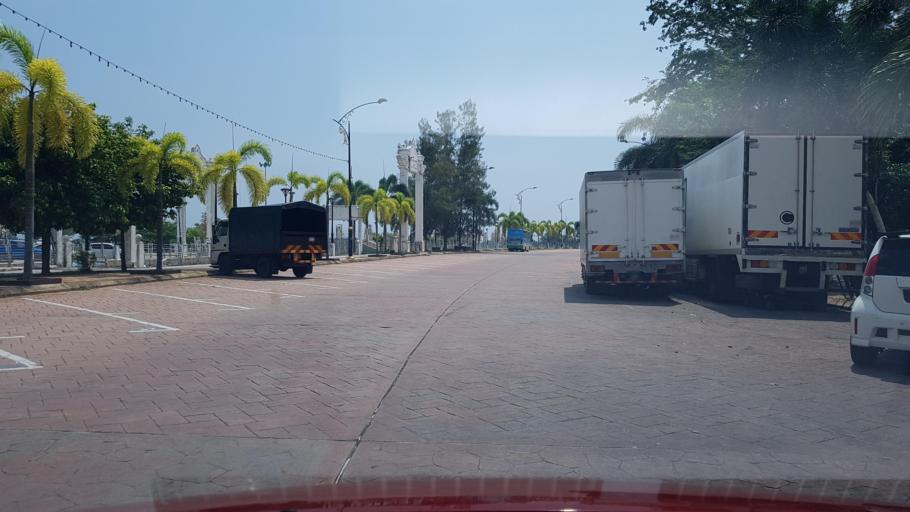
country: MY
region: Terengganu
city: Kuala Terengganu
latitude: 5.3331
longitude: 103.1321
